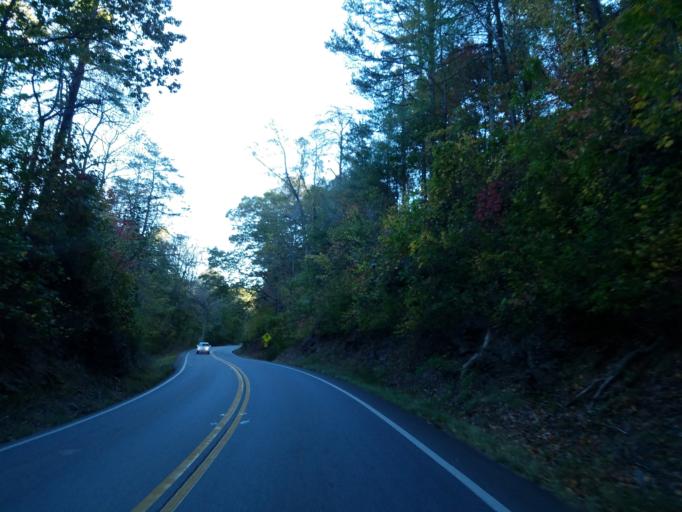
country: US
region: Georgia
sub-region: Dawson County
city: Dawsonville
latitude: 34.4279
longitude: -84.2176
